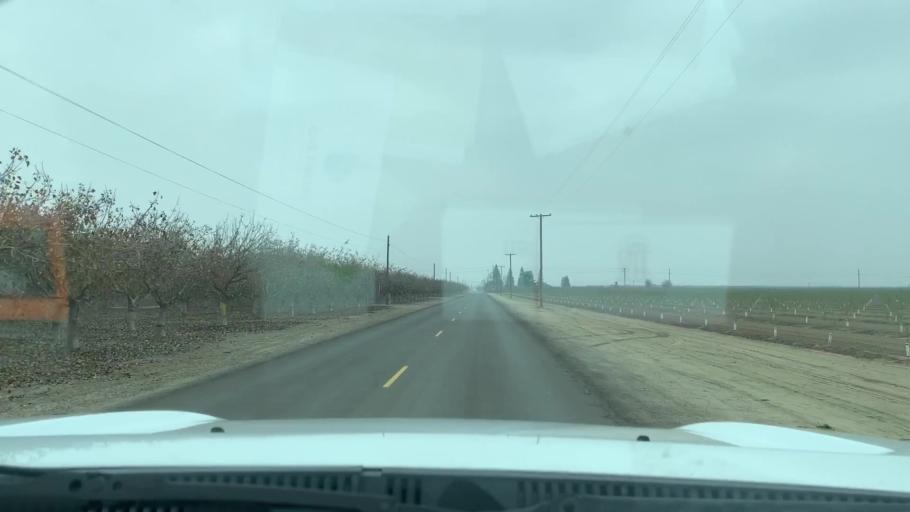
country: US
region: California
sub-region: Kern County
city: Shafter
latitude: 35.5183
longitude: -119.2959
